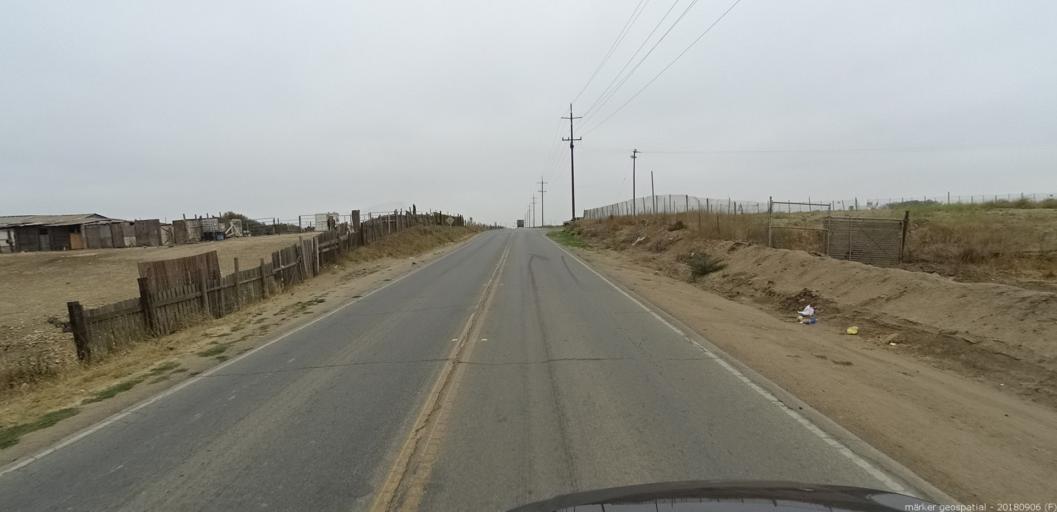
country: US
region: California
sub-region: Monterey County
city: Chualar
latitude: 36.6410
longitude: -121.5707
